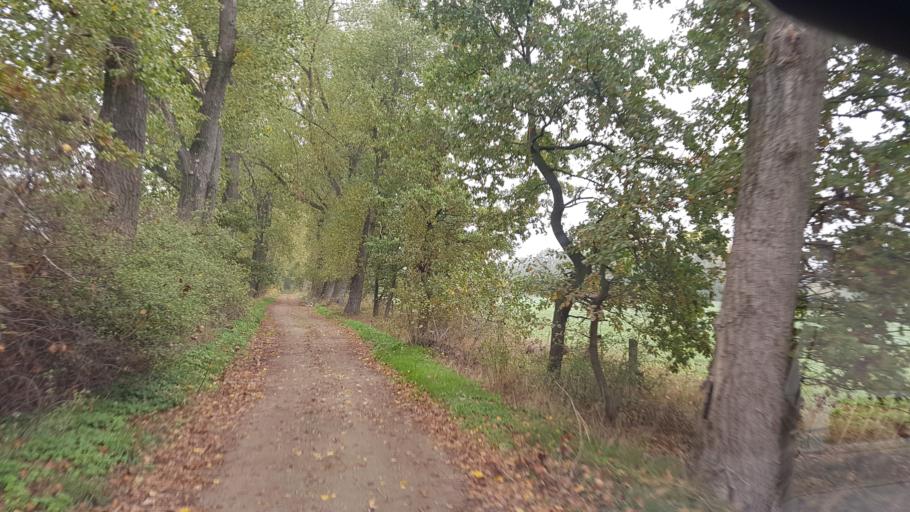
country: DE
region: Brandenburg
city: Schonewalde
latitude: 51.6891
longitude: 13.6006
